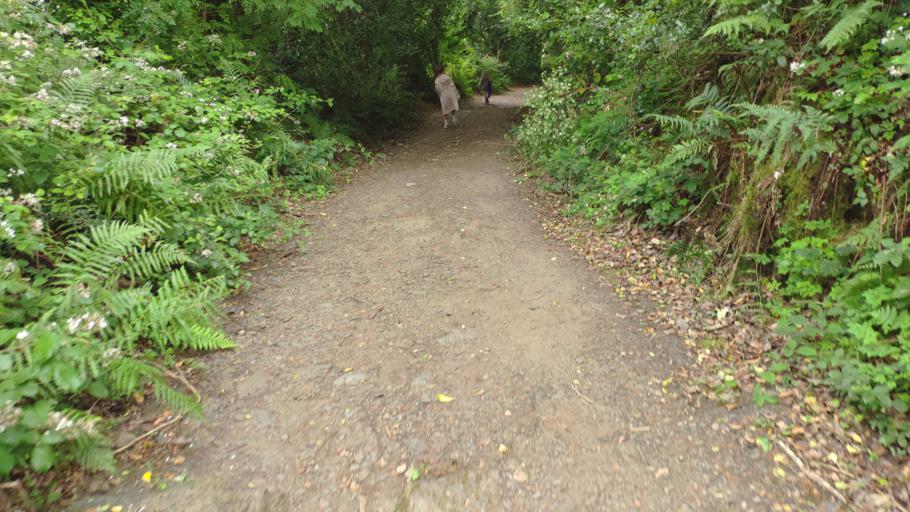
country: IE
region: Munster
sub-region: An Clar
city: Killaloe
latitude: 52.8360
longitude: -8.4713
